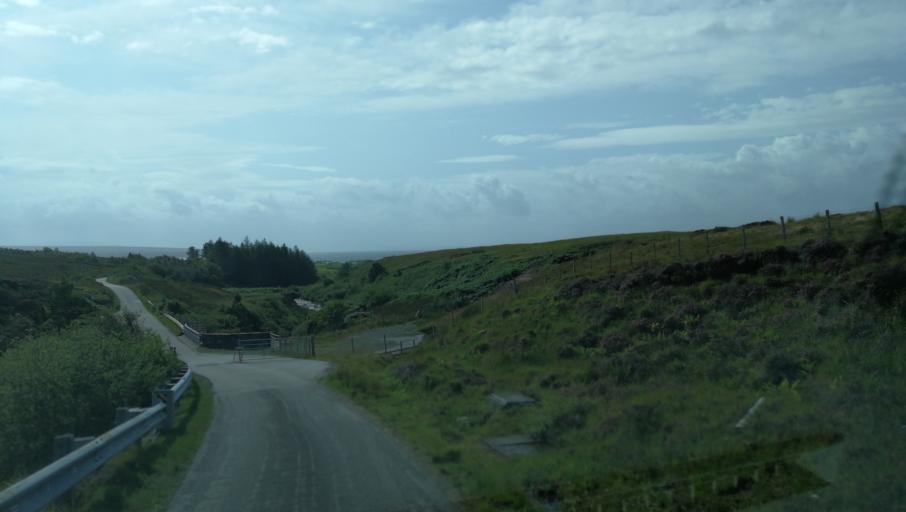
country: GB
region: Scotland
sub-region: Highland
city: Portree
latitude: 57.7486
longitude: -5.7622
